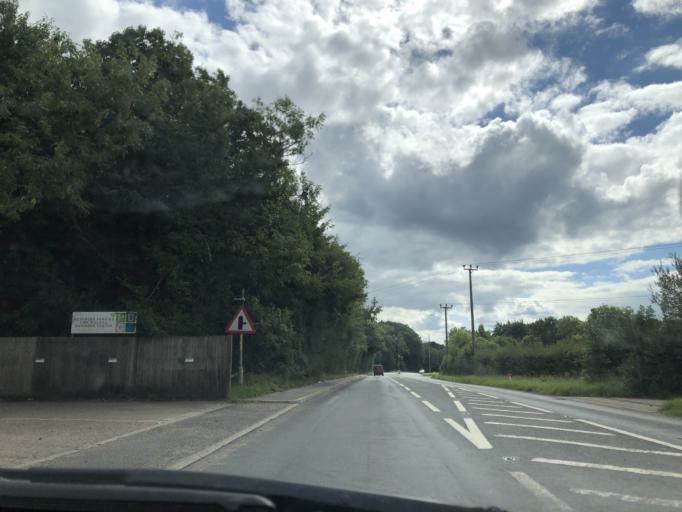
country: GB
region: England
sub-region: Kent
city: Halstead
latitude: 51.3239
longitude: 0.1557
